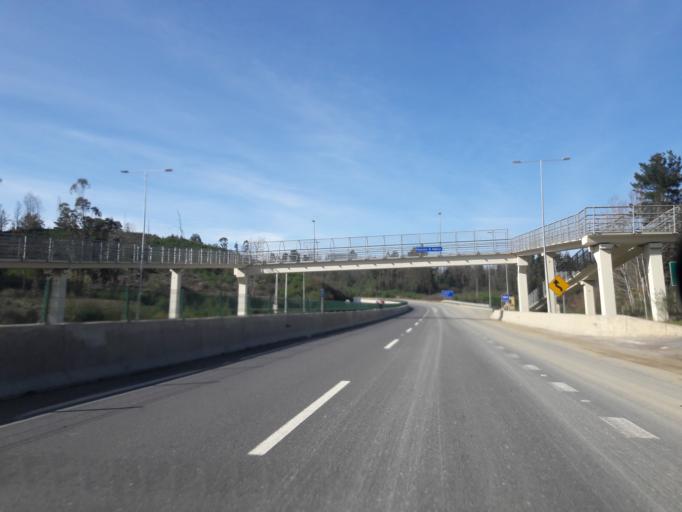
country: CL
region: Biobio
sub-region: Provincia de Concepcion
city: Chiguayante
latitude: -36.8643
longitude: -72.8541
